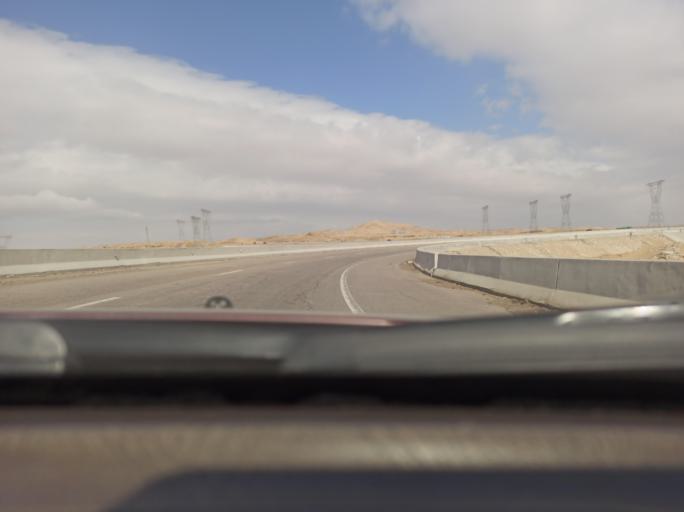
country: EG
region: Muhafazat al Fayyum
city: Tamiyah
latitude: 29.6432
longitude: 31.0117
